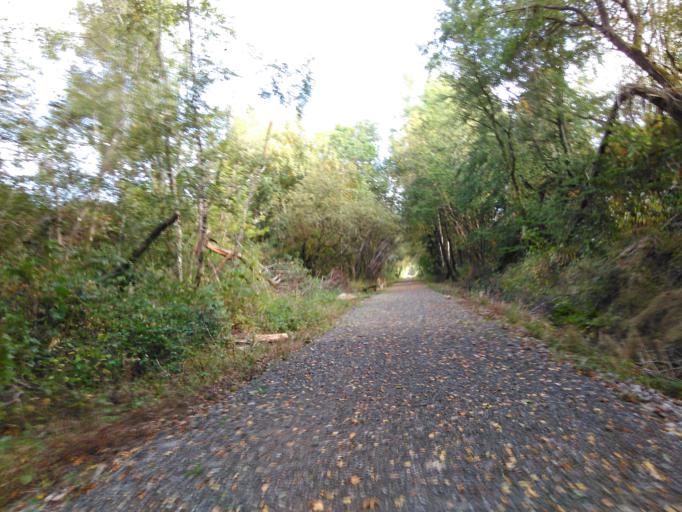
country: BE
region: Wallonia
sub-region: Province du Luxembourg
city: Vaux-sur-Sure
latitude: 49.9218
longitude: 5.5078
